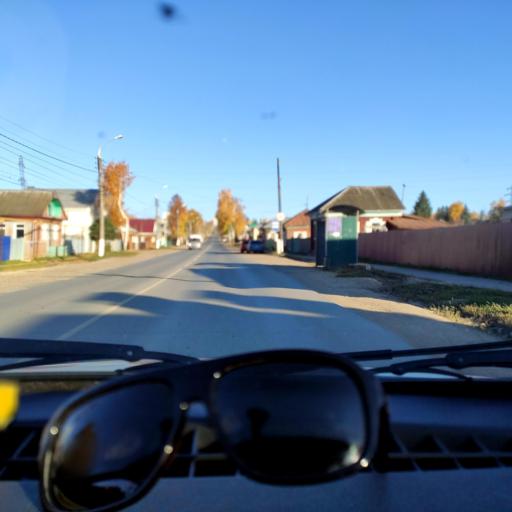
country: RU
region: Bashkortostan
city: Blagoveshchensk
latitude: 55.0362
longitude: 55.9643
